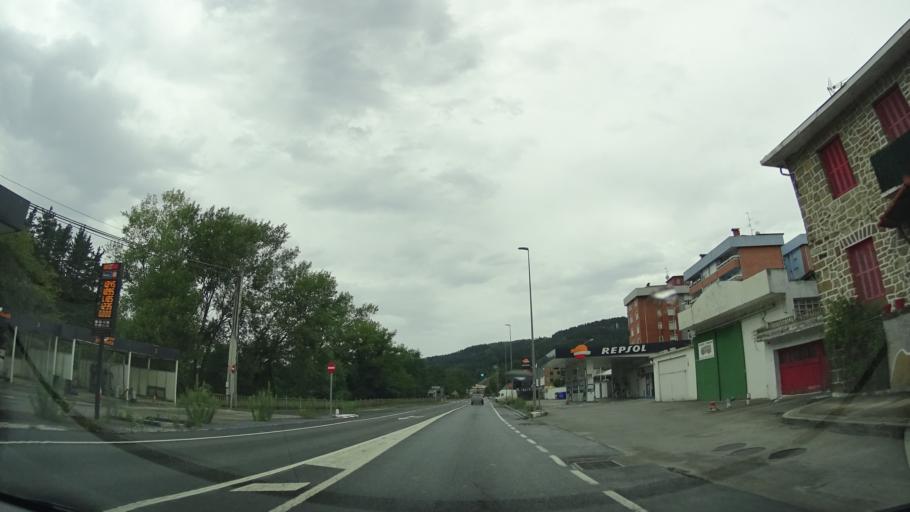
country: ES
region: Basque Country
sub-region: Bizkaia
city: Amorebieta
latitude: 43.2091
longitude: -2.7808
